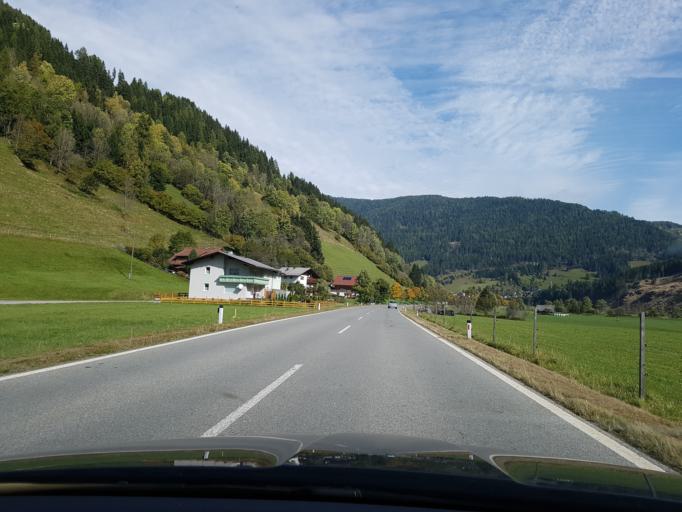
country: AT
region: Carinthia
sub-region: Politischer Bezirk Spittal an der Drau
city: Kleinkirchheim
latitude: 46.8448
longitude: 13.8814
